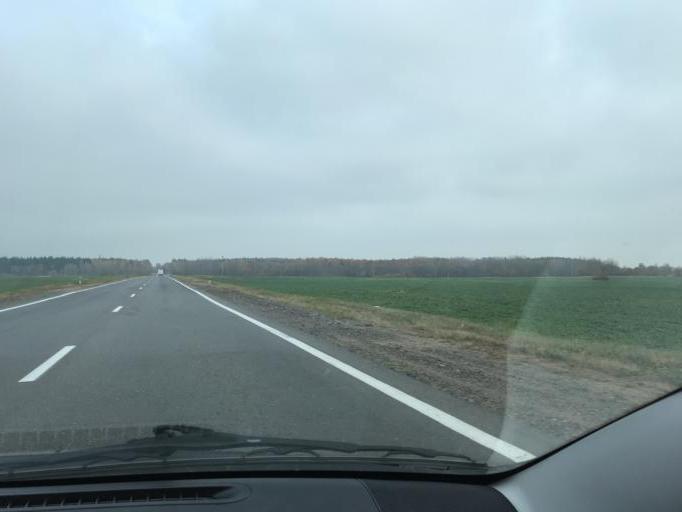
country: BY
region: Vitebsk
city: Syanno
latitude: 55.0297
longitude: 29.4914
